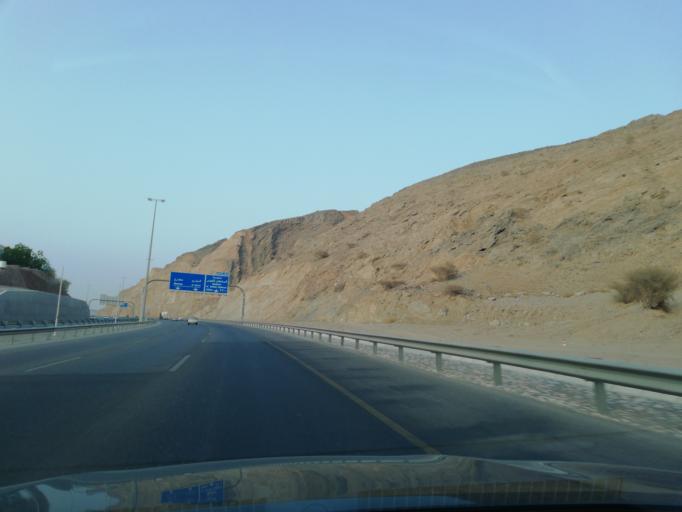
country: OM
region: Muhafazat Masqat
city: Bawshar
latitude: 23.5842
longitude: 58.4536
